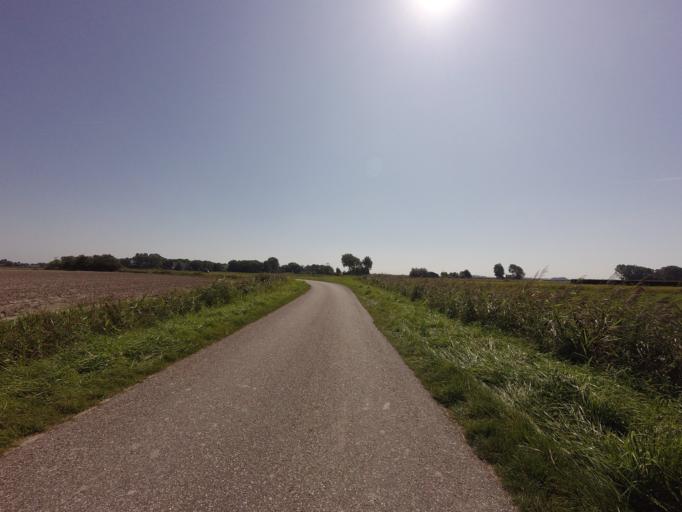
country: NL
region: Friesland
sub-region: Gemeente Dongeradeel
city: Ternaard
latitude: 53.3828
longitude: 6.0293
